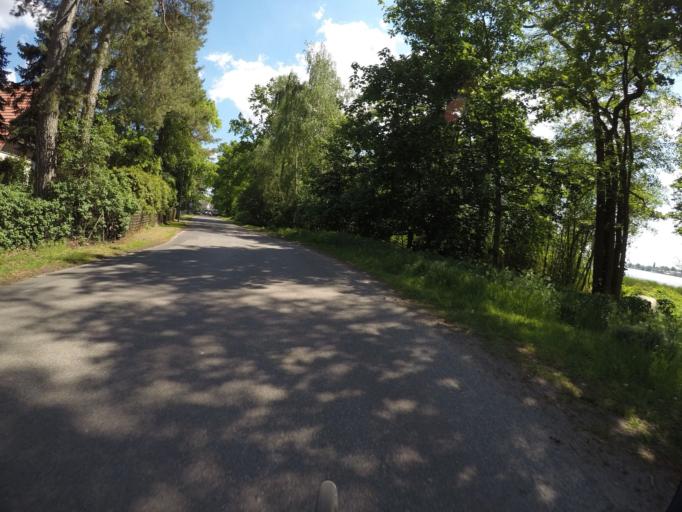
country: DE
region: Brandenburg
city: Werder
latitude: 52.3859
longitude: 12.9534
